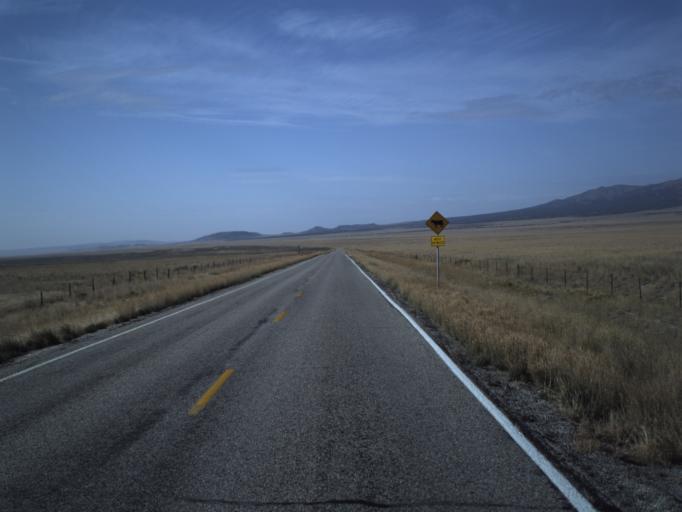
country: US
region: Idaho
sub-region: Oneida County
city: Malad City
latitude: 41.9623
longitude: -113.0642
